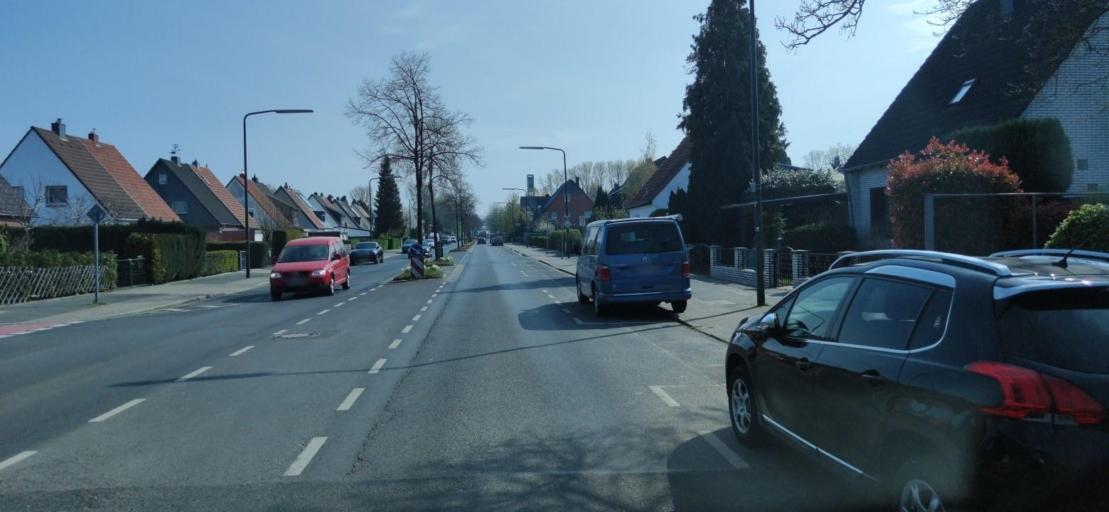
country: DE
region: North Rhine-Westphalia
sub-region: Regierungsbezirk Dusseldorf
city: Erkrath
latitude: 51.2136
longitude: 6.8496
